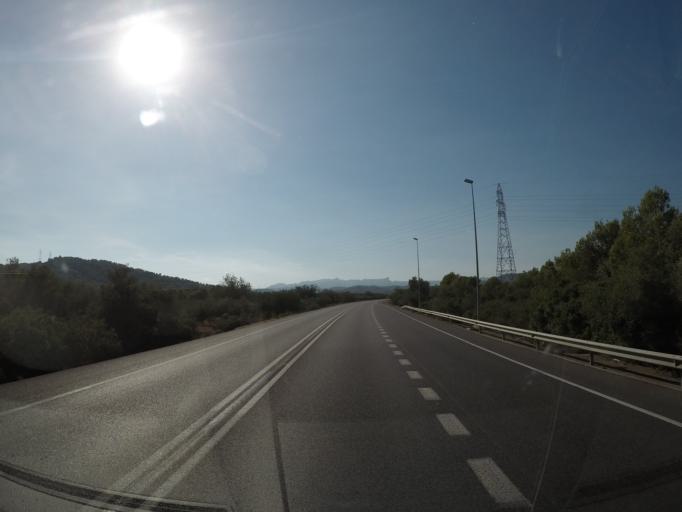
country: ES
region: Catalonia
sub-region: Provincia de Tarragona
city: El Perello
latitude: 40.8969
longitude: 0.7458
